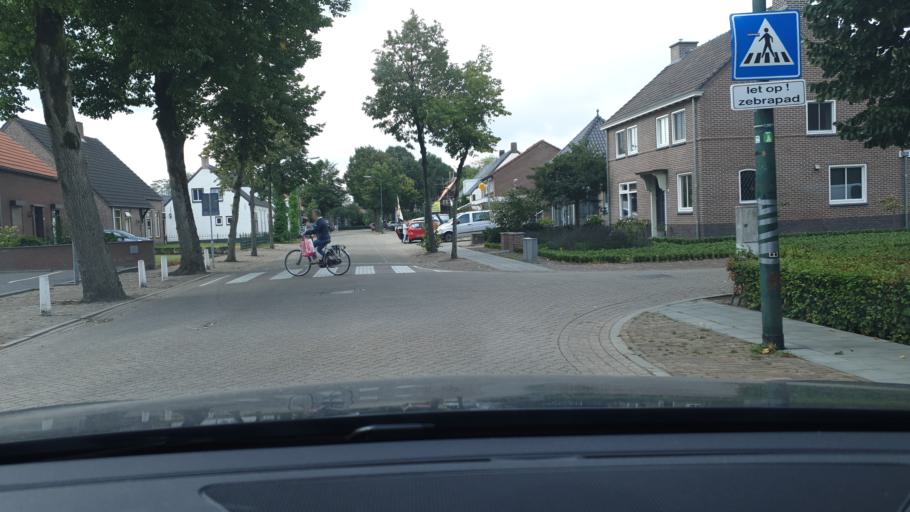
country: NL
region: North Brabant
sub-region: Gemeente Veldhoven
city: Oerle
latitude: 51.4426
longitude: 5.3396
